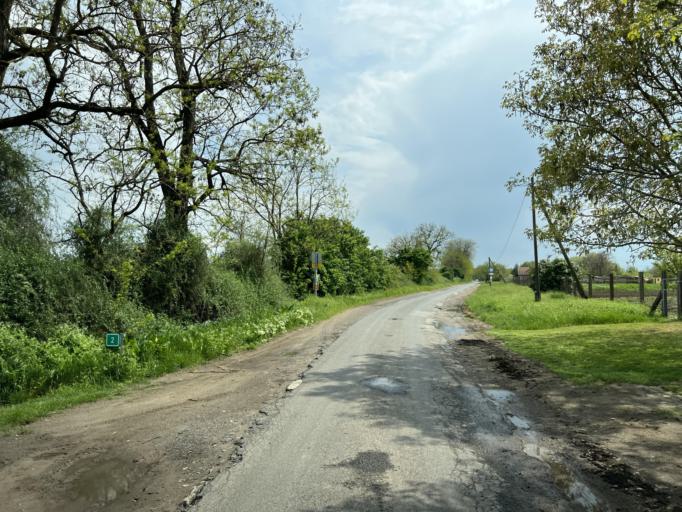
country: HU
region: Pest
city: Nagykoros
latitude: 47.0139
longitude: 19.7937
